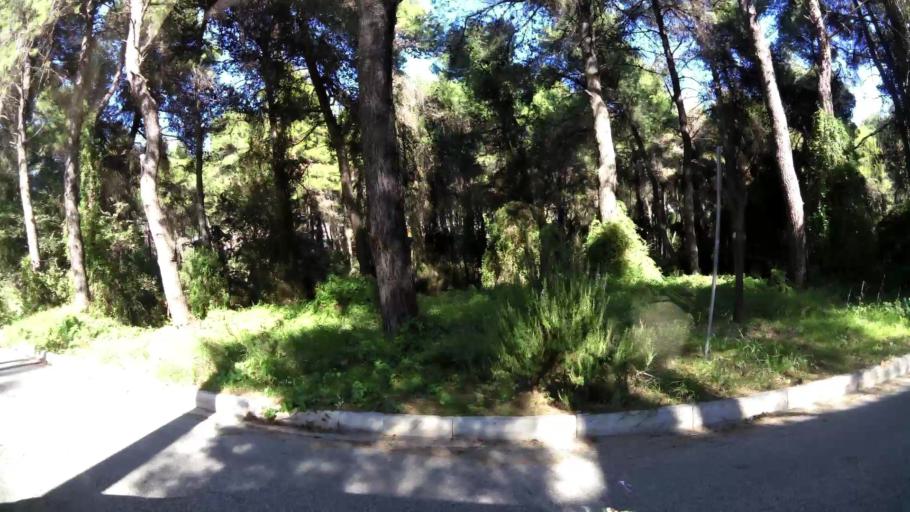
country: GR
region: Attica
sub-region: Nomarchia Athinas
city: Ekali
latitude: 38.1152
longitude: 23.8394
